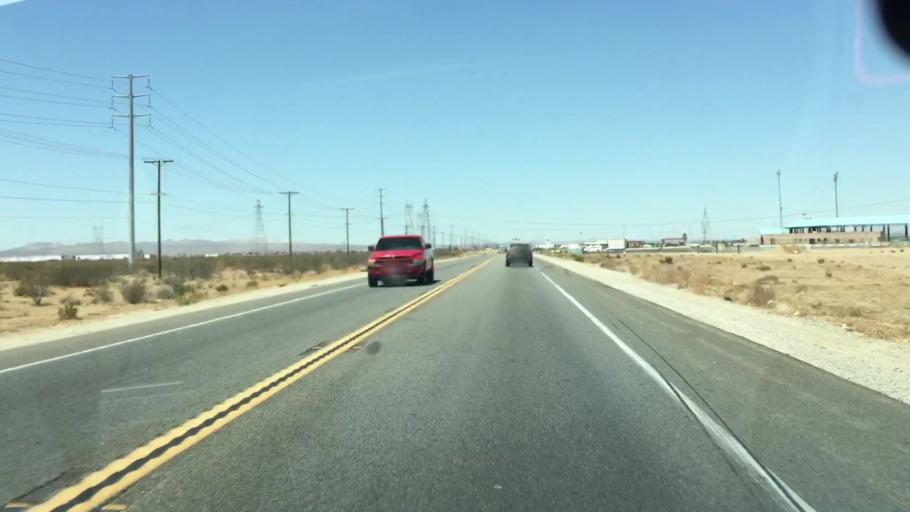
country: US
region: California
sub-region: San Bernardino County
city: Adelanto
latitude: 34.5510
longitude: -117.4024
